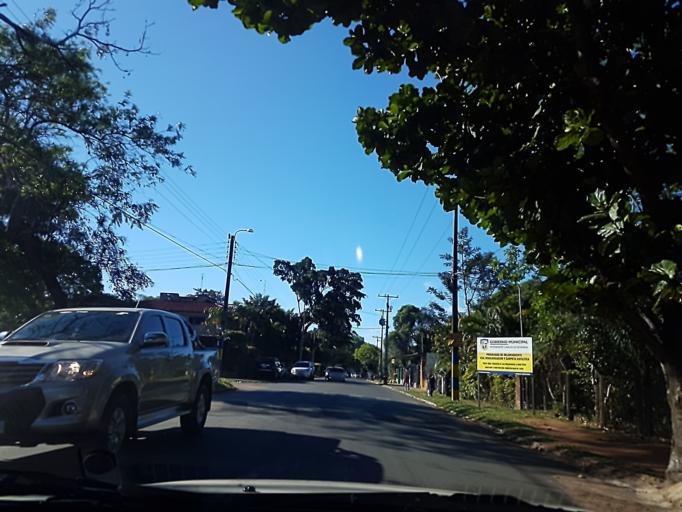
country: PY
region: Central
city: San Lorenzo
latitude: -25.2786
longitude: -57.4736
